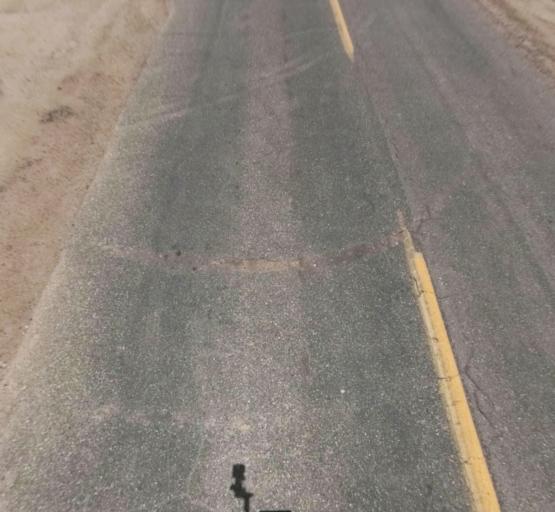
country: US
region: California
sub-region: Madera County
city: Parkwood
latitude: 36.9067
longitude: -120.0924
